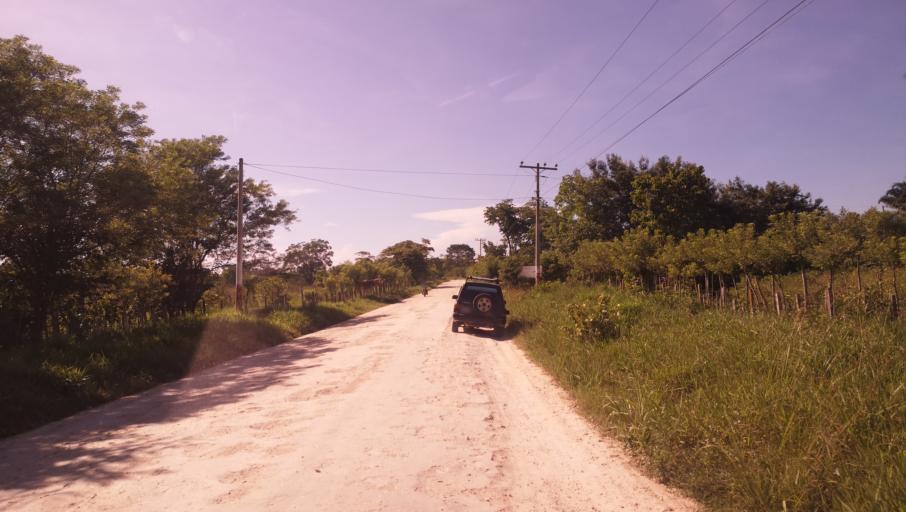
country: GT
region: Peten
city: Dolores
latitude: 16.7169
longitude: -89.3693
